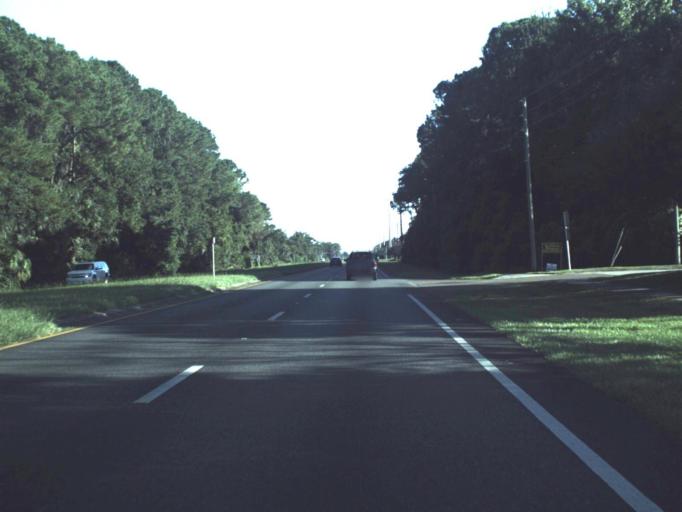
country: US
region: Florida
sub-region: Citrus County
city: Crystal River
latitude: 28.8630
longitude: -82.5798
